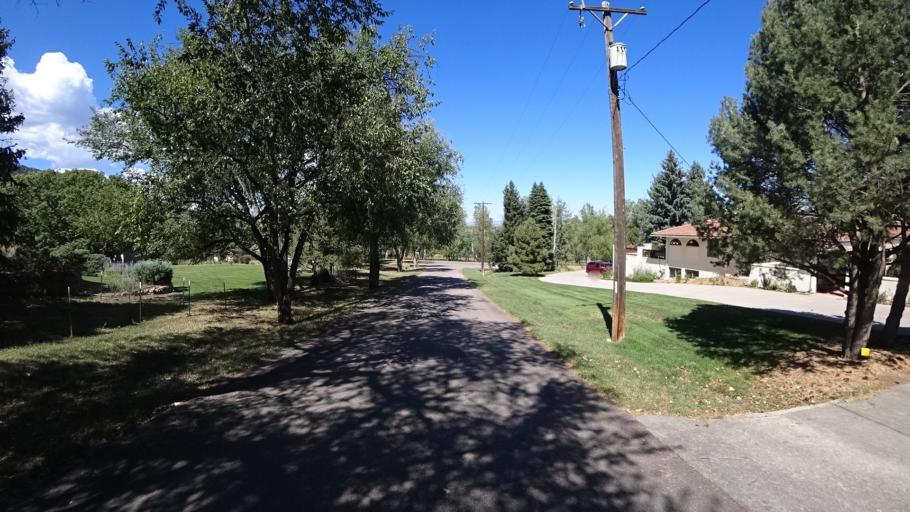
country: US
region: Colorado
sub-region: El Paso County
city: Colorado Springs
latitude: 38.7860
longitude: -104.8597
